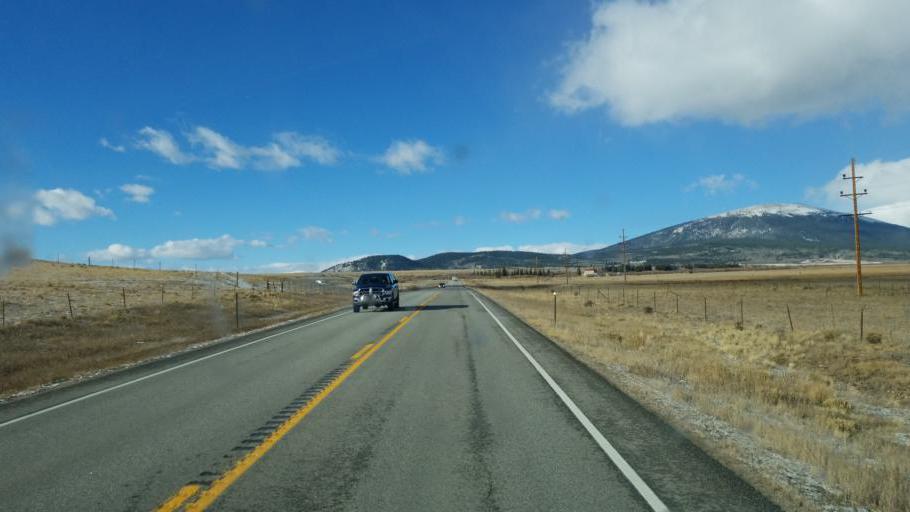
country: US
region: Colorado
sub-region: Park County
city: Fairplay
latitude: 39.3374
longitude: -105.8589
